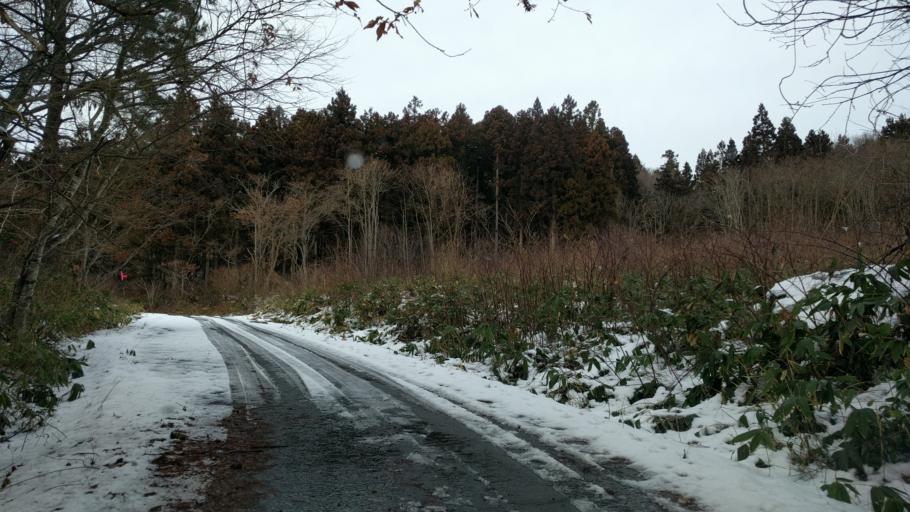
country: JP
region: Fukushima
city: Inawashiro
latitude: 37.5739
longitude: 139.9951
